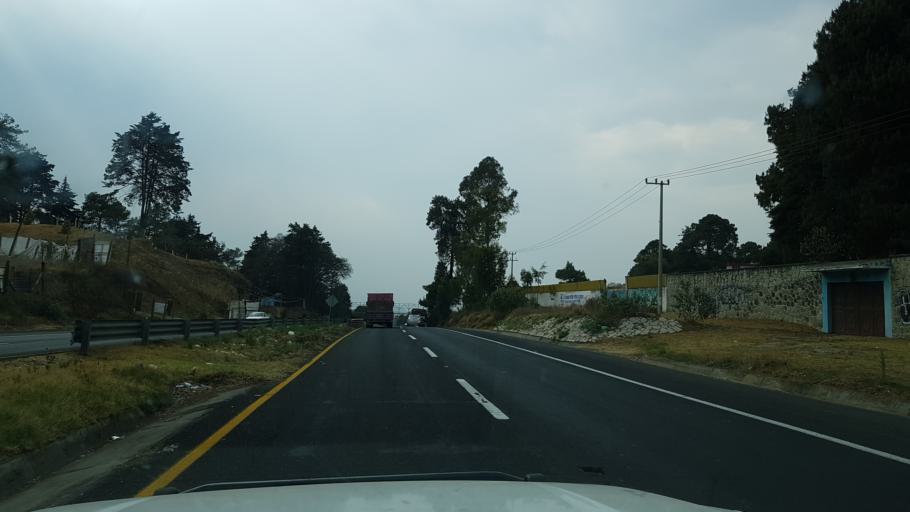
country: MX
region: Mexico
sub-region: Tlalmanalco
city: Santo Tomas Atzingo
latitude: 19.1854
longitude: -98.7953
